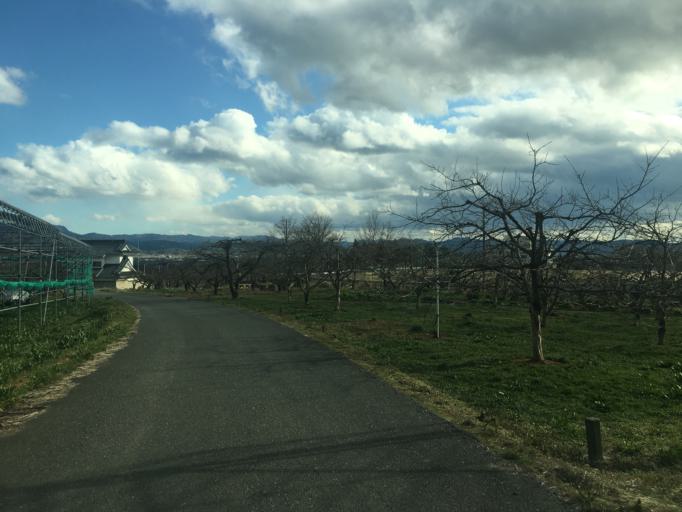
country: JP
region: Fukushima
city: Yanagawamachi-saiwaicho
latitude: 37.8910
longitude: 140.5728
